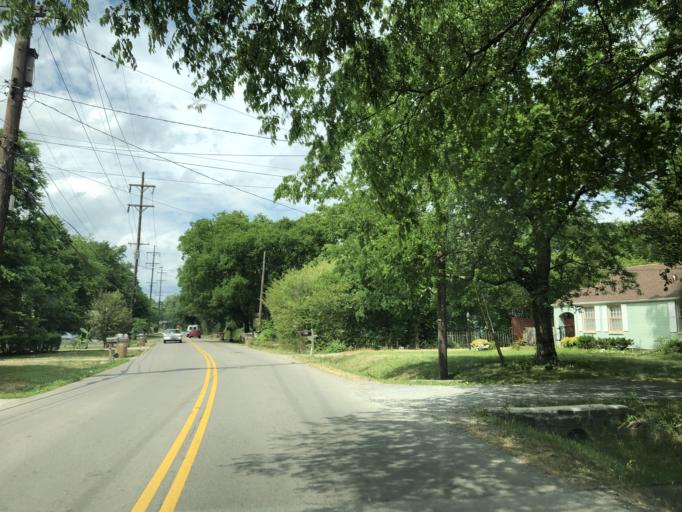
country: US
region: Tennessee
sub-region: Davidson County
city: Goodlettsville
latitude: 36.2650
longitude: -86.7041
